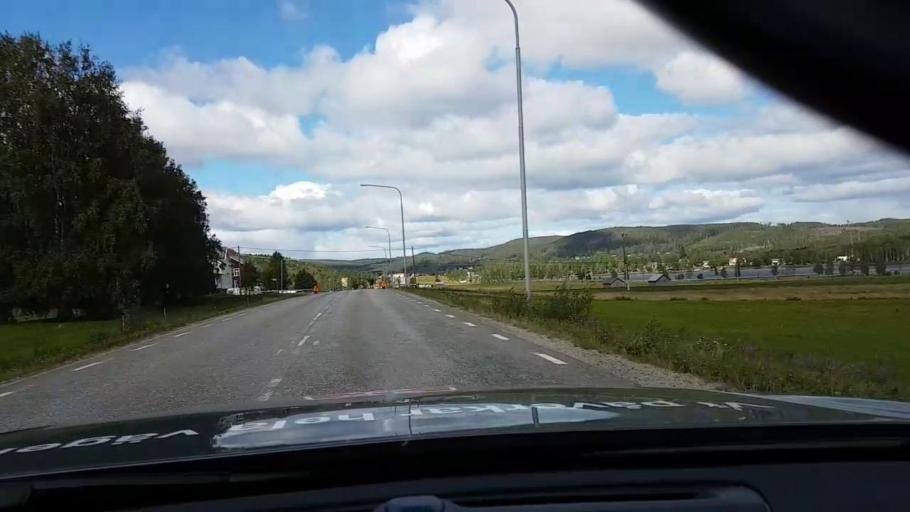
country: SE
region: Vaesternorrland
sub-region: OErnskoeldsviks Kommun
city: Bredbyn
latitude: 63.5006
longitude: 18.0793
